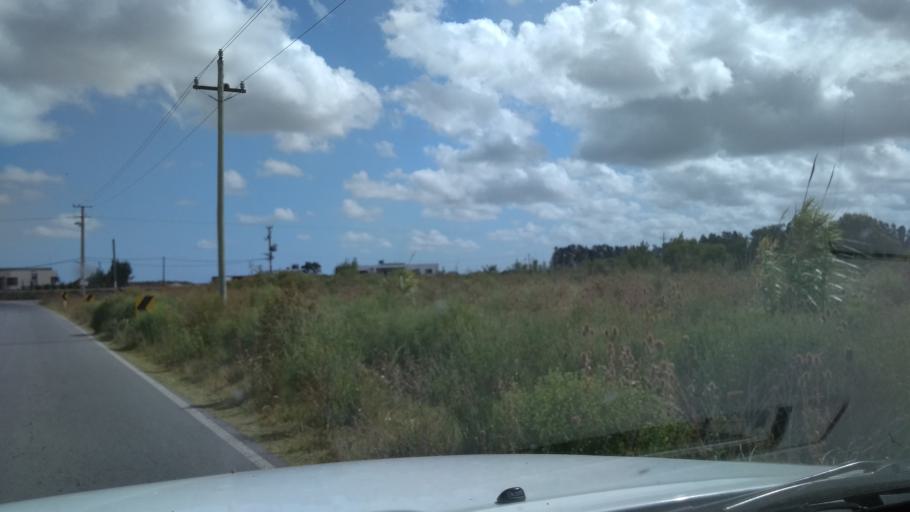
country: UY
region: Canelones
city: Colonia Nicolich
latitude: -34.7822
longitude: -56.0196
